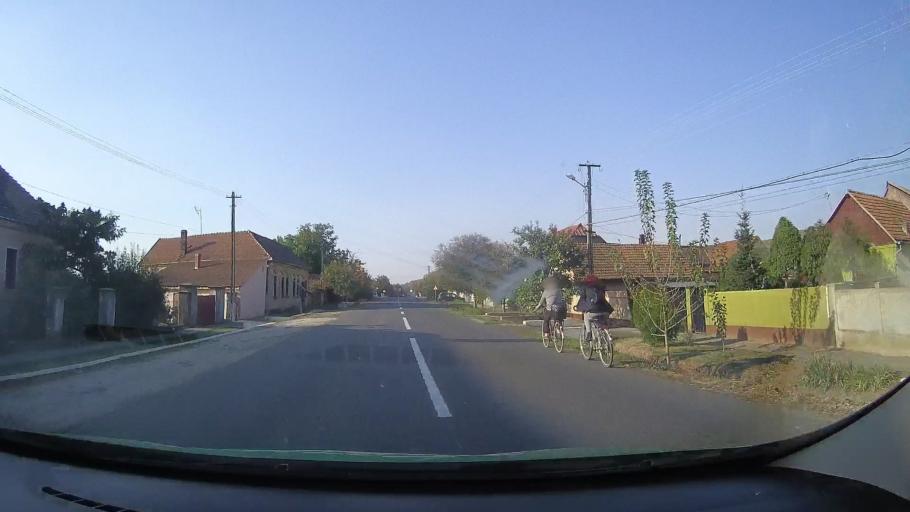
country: RO
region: Arad
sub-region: Comuna Ghioroc
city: Ghioroc
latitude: 46.1386
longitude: 21.6042
